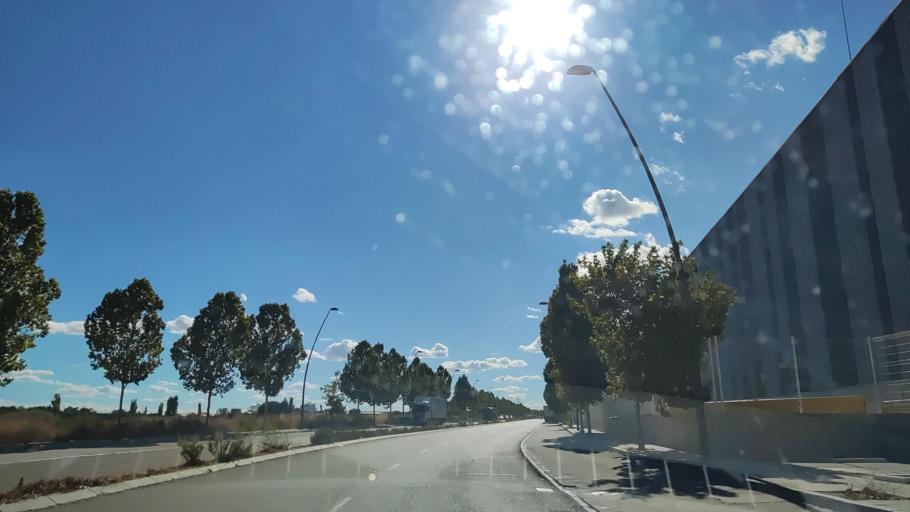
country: ES
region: Madrid
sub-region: Provincia de Madrid
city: Pinto
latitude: 40.2780
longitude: -3.6754
